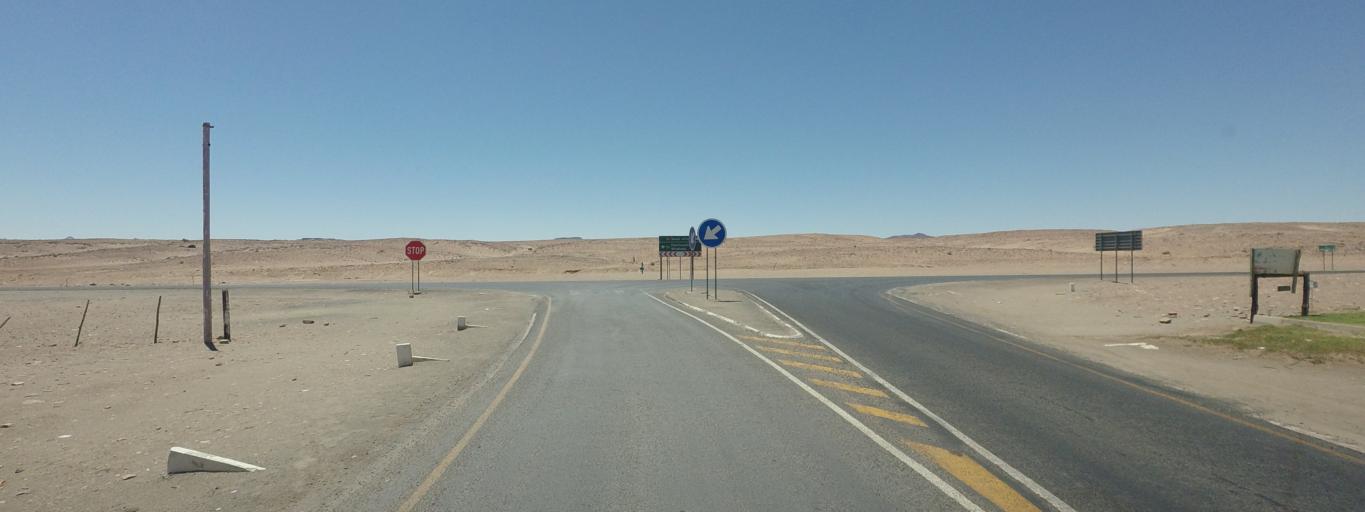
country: ZA
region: Northern Cape
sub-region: Namakwa District Municipality
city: Port Nolloth
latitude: -28.7361
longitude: 17.6166
